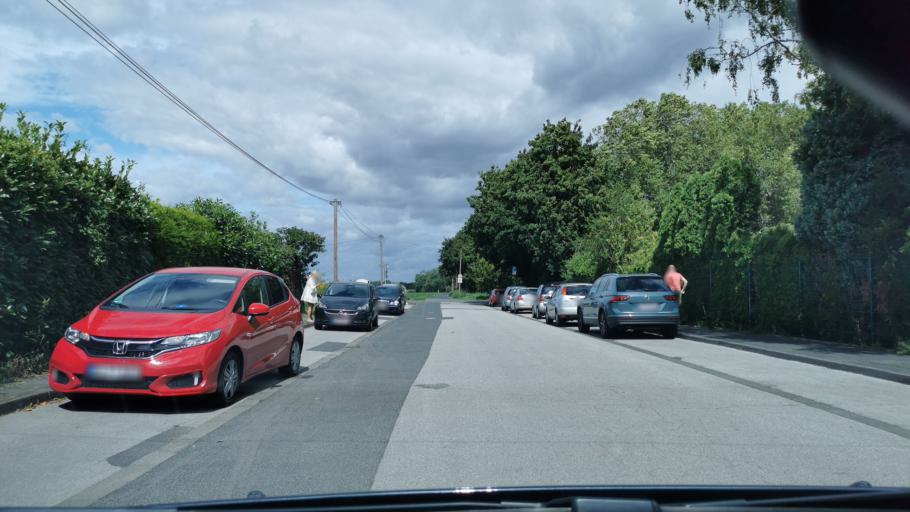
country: DE
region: North Rhine-Westphalia
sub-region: Regierungsbezirk Koln
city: Hurth
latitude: 50.9029
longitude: 6.8881
